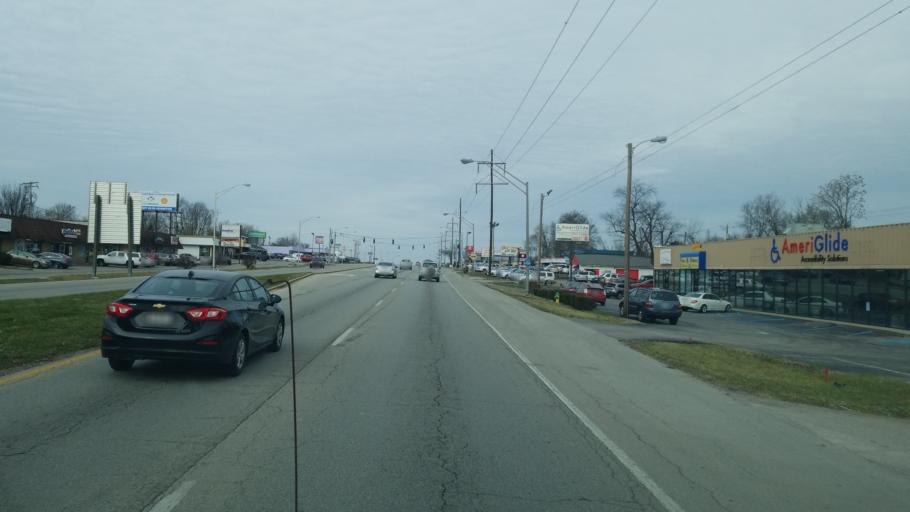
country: US
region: Kentucky
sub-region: Fayette County
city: Lexington-Fayette
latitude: 38.0545
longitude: -84.4594
